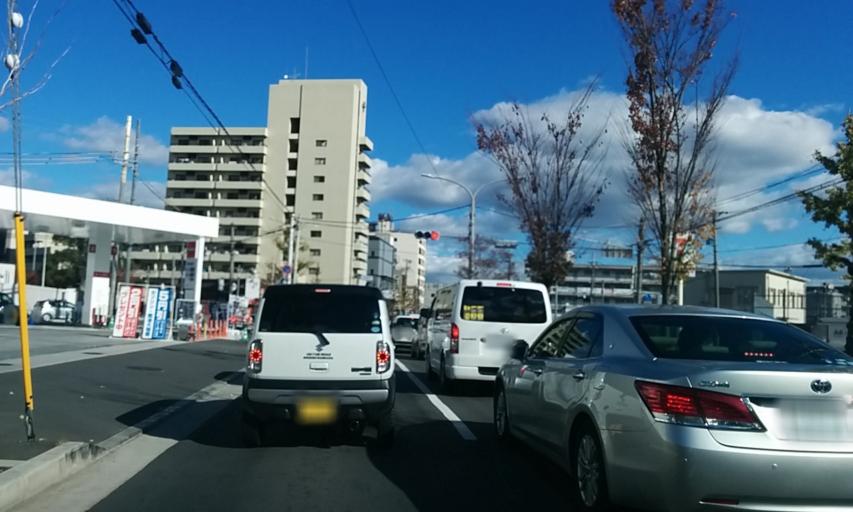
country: JP
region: Kyoto
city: Kyoto
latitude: 34.9688
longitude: 135.7565
